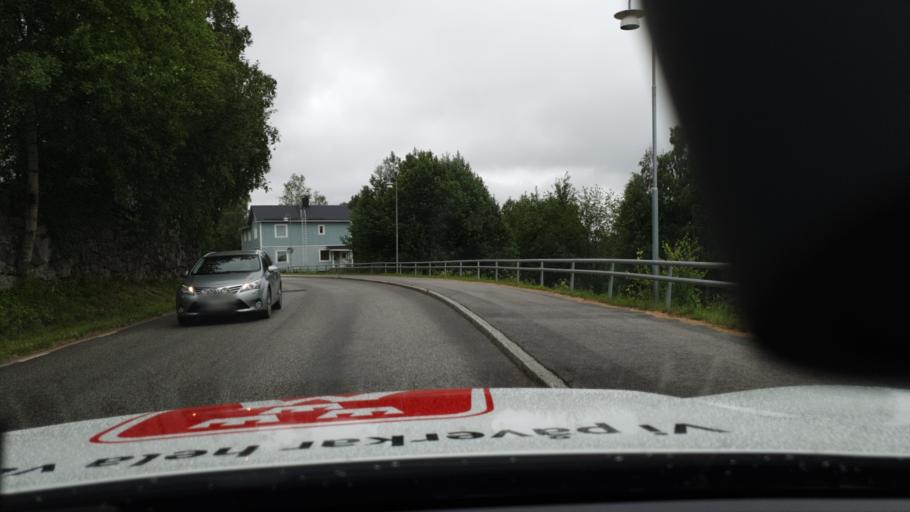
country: SE
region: Norrbotten
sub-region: Overtornea Kommun
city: OEvertornea
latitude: 66.3934
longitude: 23.6542
